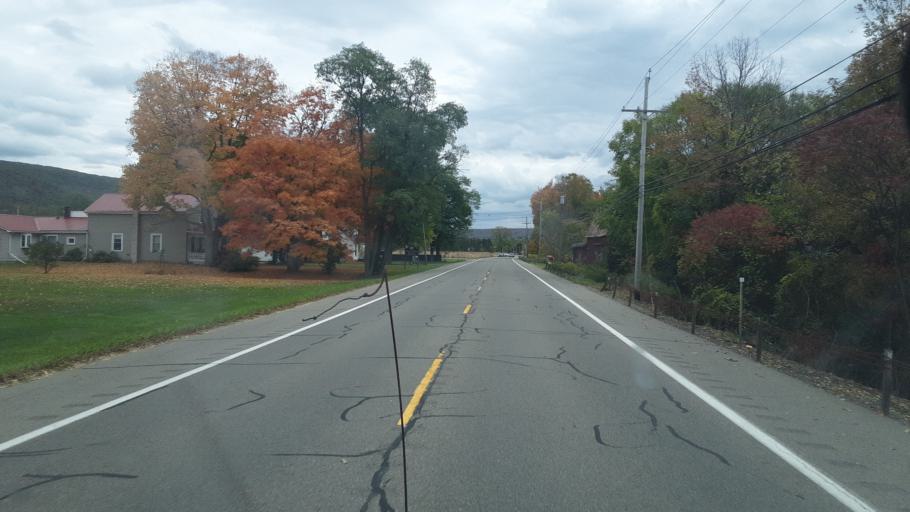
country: US
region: New York
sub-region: Allegany County
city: Belmont
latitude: 42.2027
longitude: -78.0055
